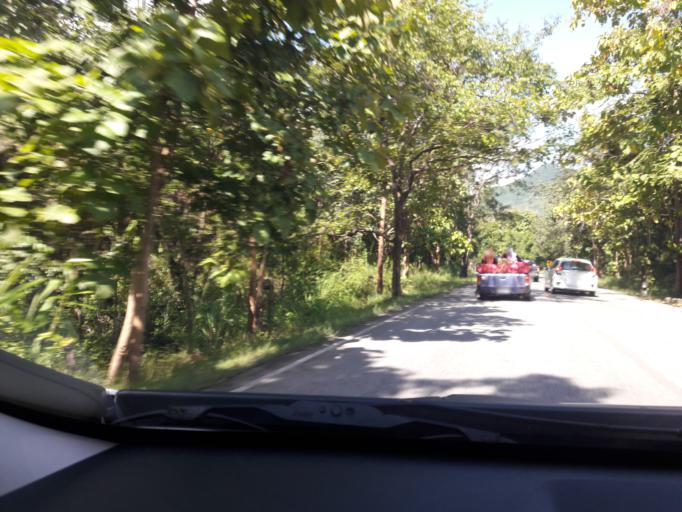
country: TH
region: Mae Hong Son
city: Mae Hi
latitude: 19.3093
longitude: 98.4528
